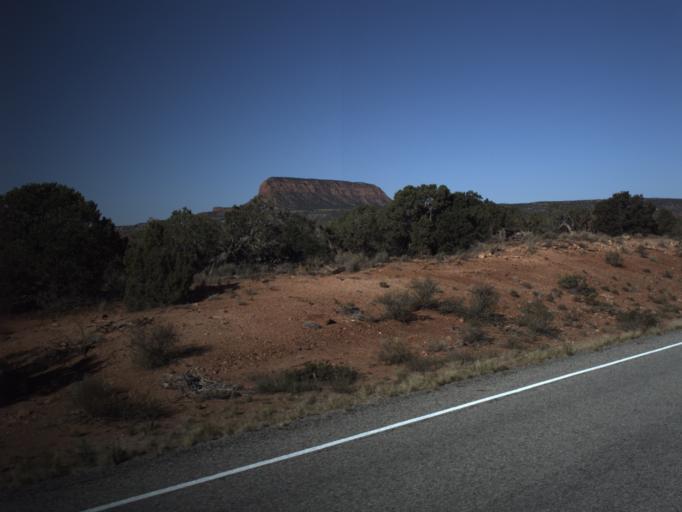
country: US
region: Utah
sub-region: San Juan County
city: Blanding
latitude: 37.5495
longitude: -109.9896
